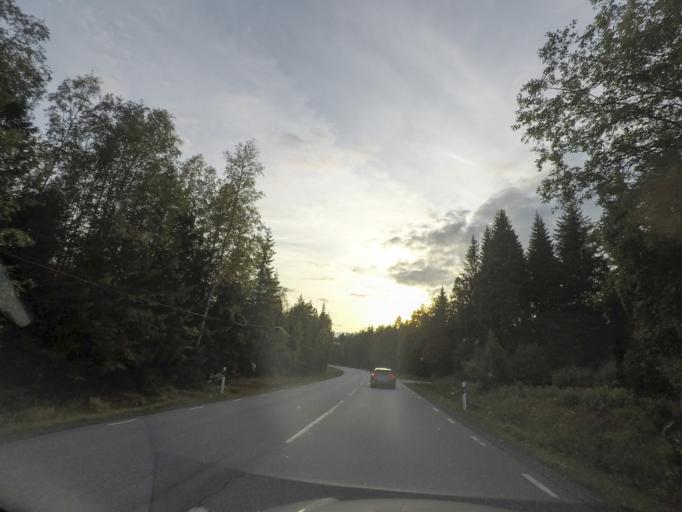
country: SE
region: OErebro
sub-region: Nora Kommun
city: As
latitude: 59.5189
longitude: 14.9401
